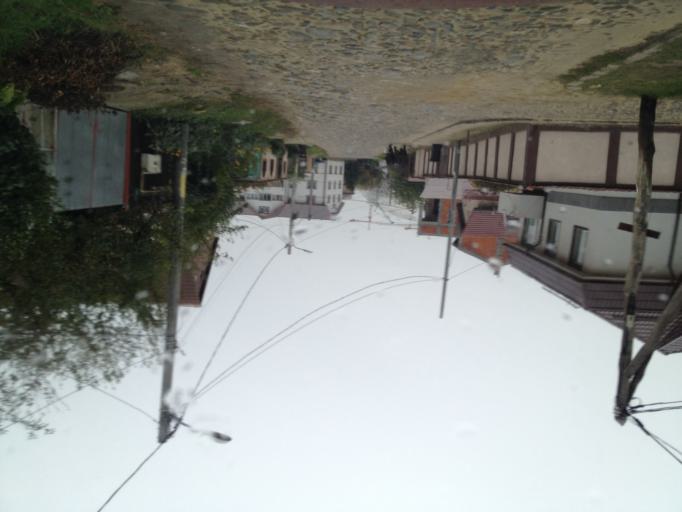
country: RO
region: Dolj
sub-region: Municipiul Craiova
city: Mofleni
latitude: 44.3117
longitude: 23.7765
